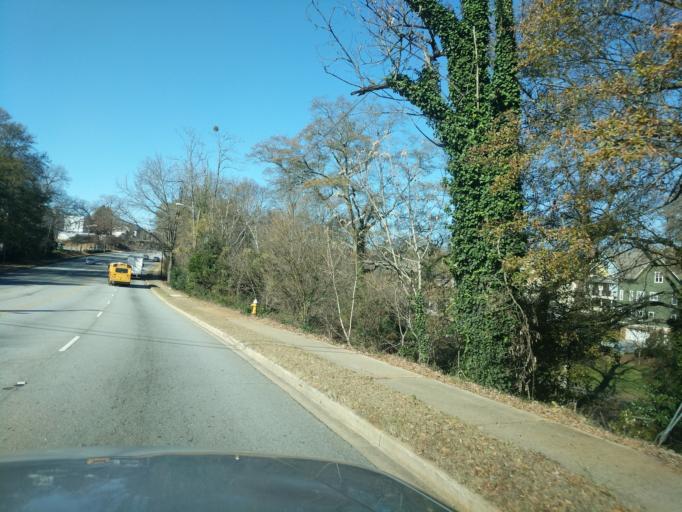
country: US
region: South Carolina
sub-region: Greenville County
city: Greenville
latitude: 34.8557
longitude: -82.3916
